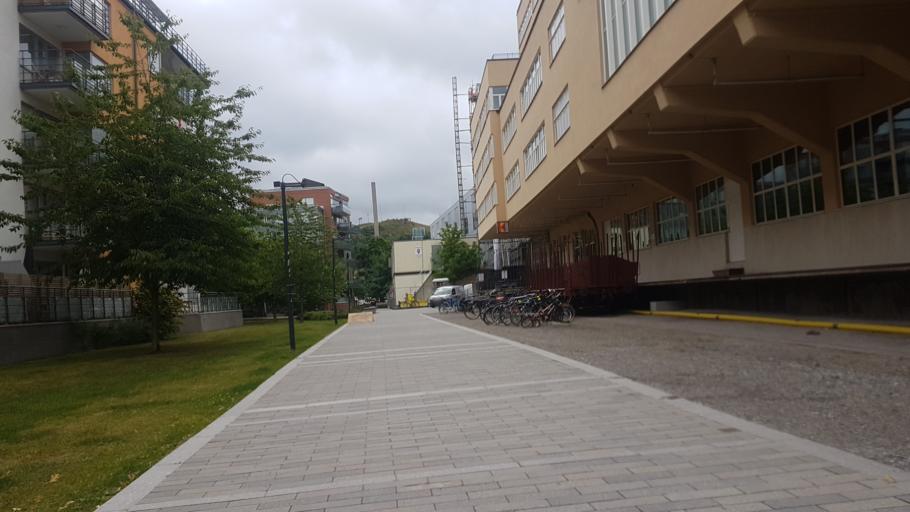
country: SE
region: Stockholm
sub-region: Stockholms Kommun
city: OEstermalm
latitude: 59.3025
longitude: 18.0976
